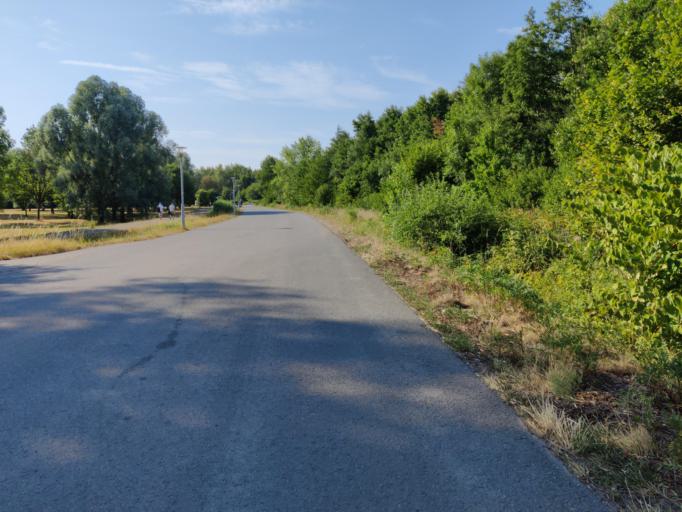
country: DE
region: Saxony
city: Markkleeberg
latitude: 51.2846
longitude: 12.3479
